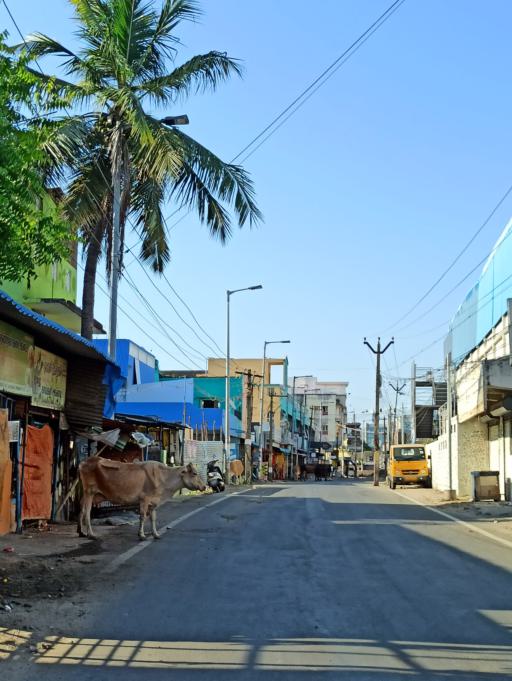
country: IN
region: Tamil Nadu
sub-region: Kancheepuram
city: Manappakkam
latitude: 13.0229
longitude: 80.1674
